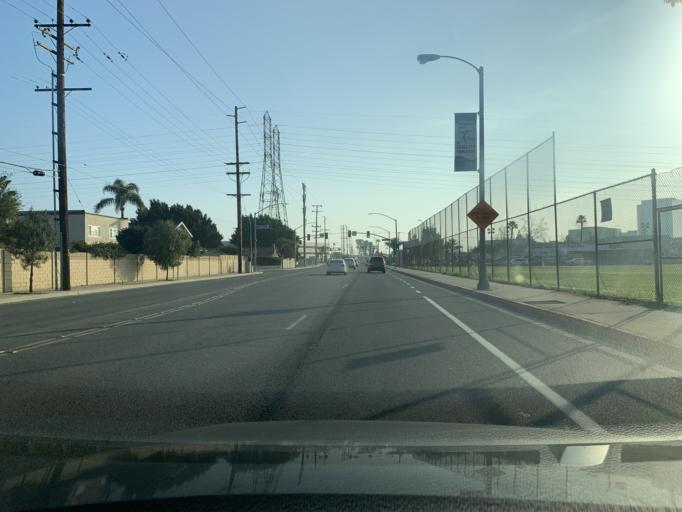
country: US
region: California
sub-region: Orange County
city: Midway City
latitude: 33.7374
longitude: -118.0005
